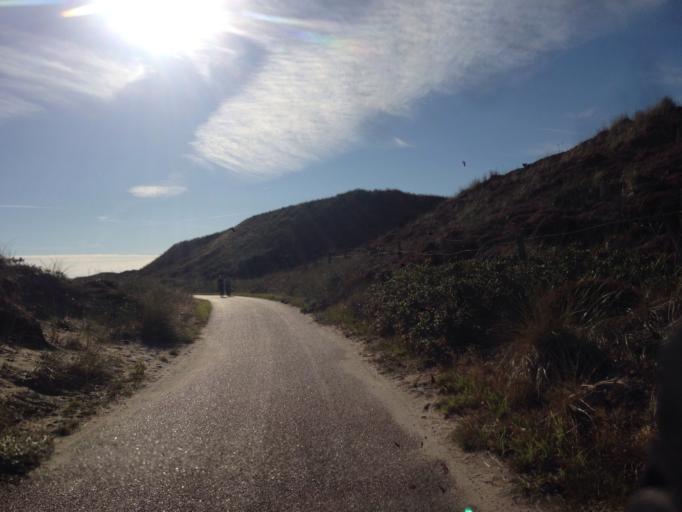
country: DE
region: Schleswig-Holstein
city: List
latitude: 55.0026
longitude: 8.3682
